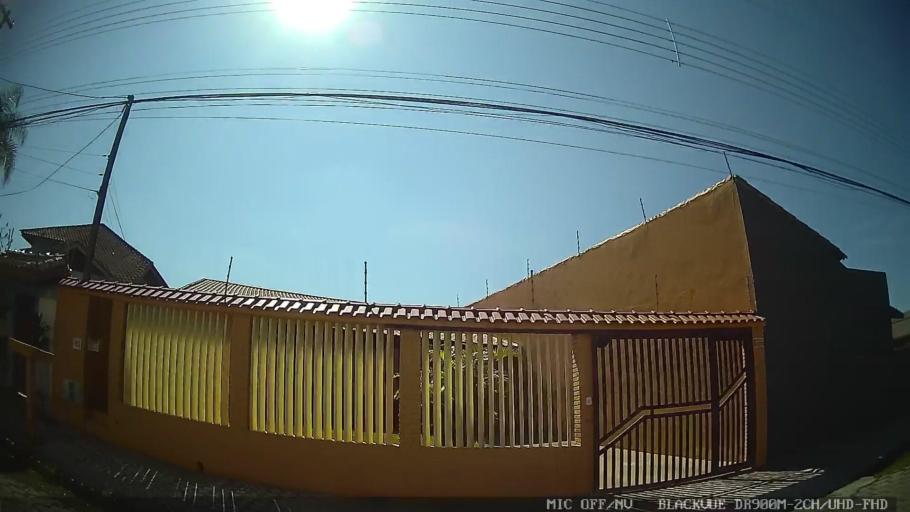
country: BR
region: Sao Paulo
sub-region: Peruibe
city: Peruibe
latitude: -24.2998
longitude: -46.9693
